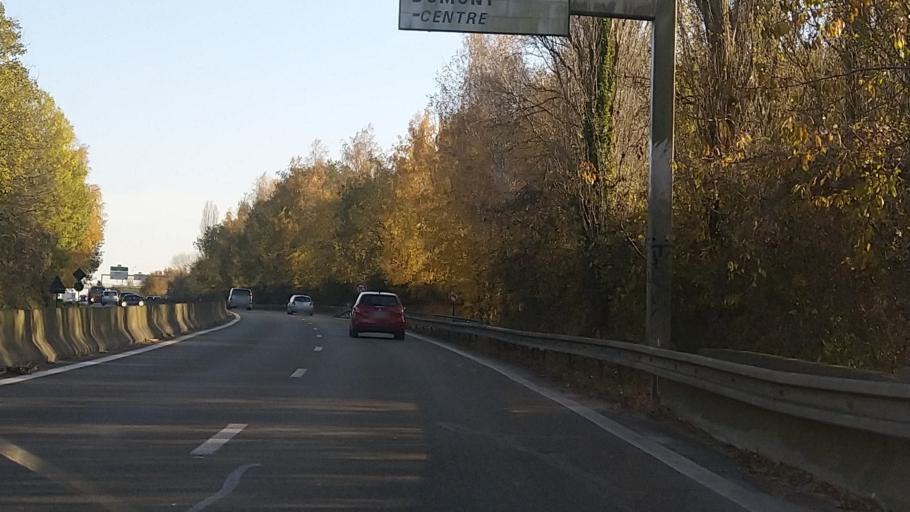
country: FR
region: Ile-de-France
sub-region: Departement du Val-d'Oise
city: Moisselles
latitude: 49.0477
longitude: 2.3323
